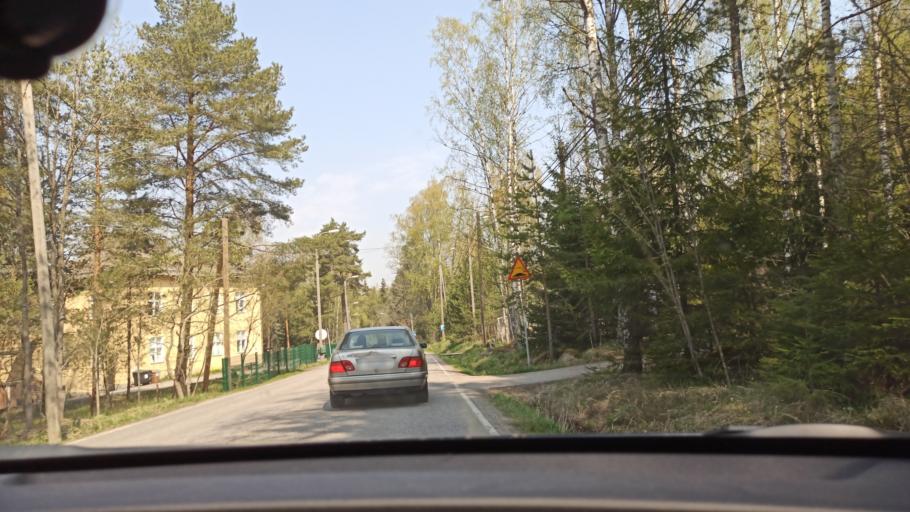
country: FI
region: Uusimaa
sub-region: Helsinki
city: Kirkkonummi
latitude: 60.0989
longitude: 24.5655
